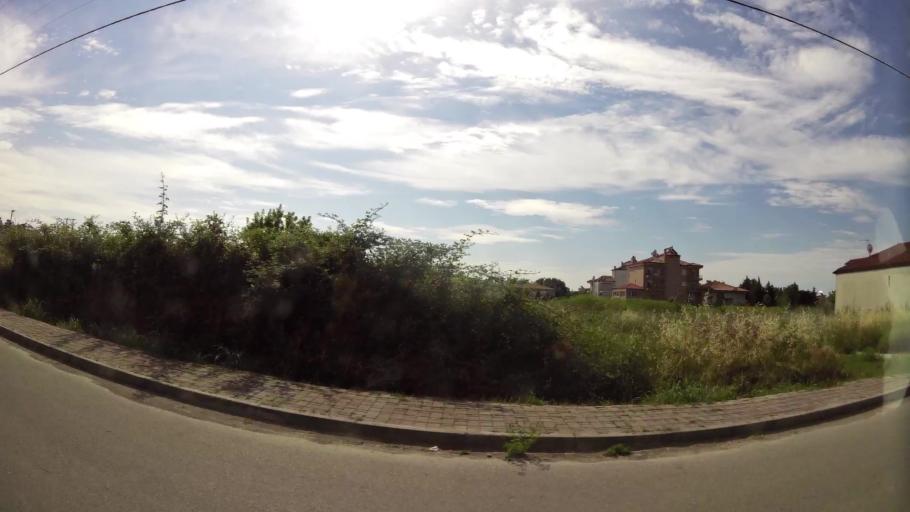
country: GR
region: Central Macedonia
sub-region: Nomos Pierias
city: Katerini
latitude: 40.2818
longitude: 22.5137
